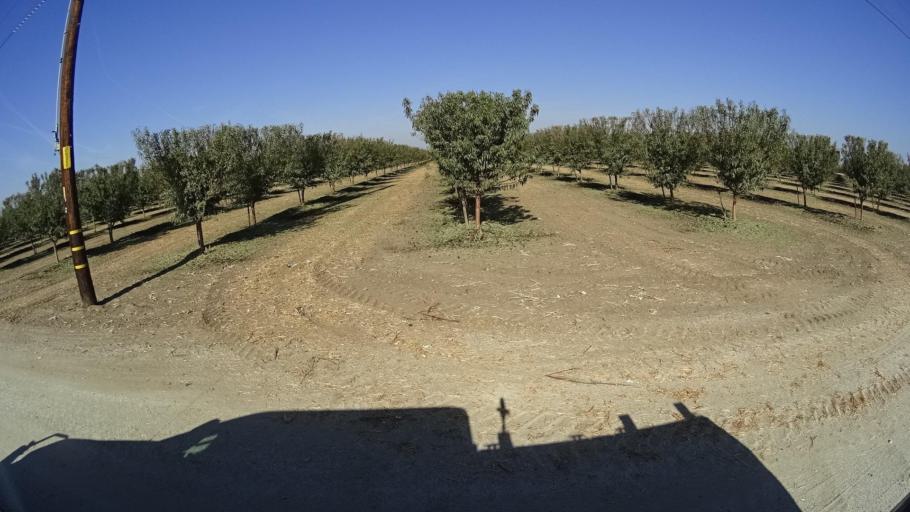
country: US
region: California
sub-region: Kern County
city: McFarland
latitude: 35.7034
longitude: -119.2015
